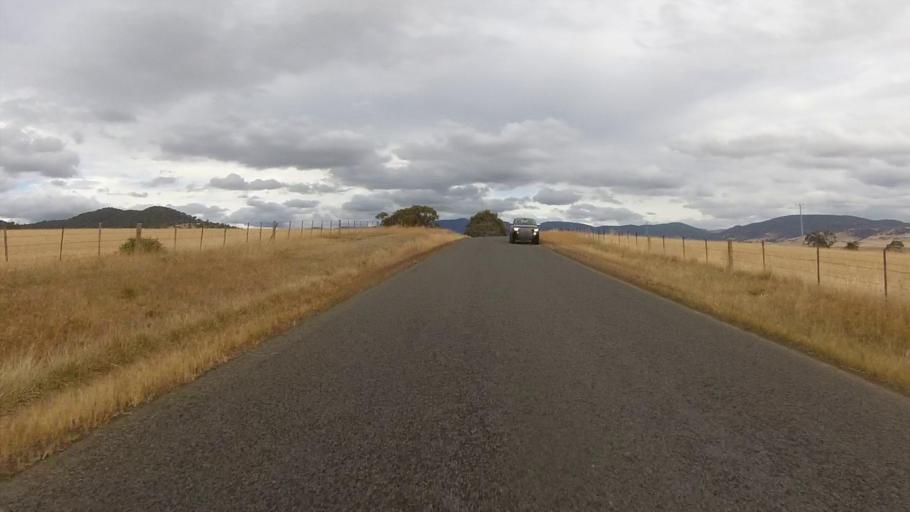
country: AU
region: Tasmania
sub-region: Northern Midlands
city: Evandale
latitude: -41.7934
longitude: 147.7443
